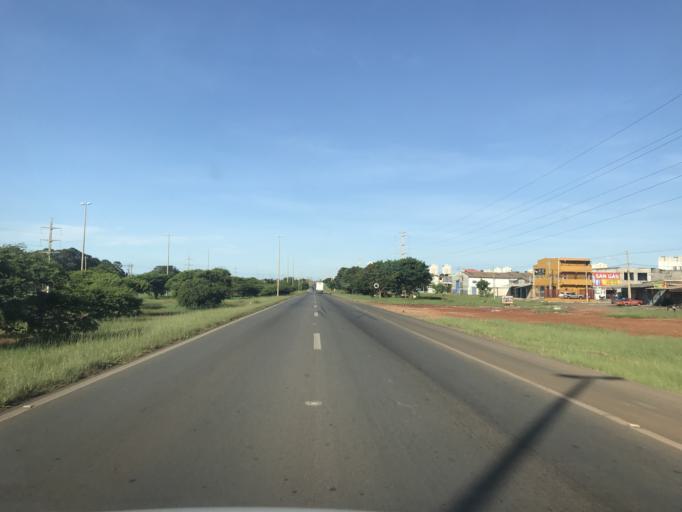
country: BR
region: Federal District
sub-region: Brasilia
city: Brasilia
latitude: -15.8850
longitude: -48.0704
